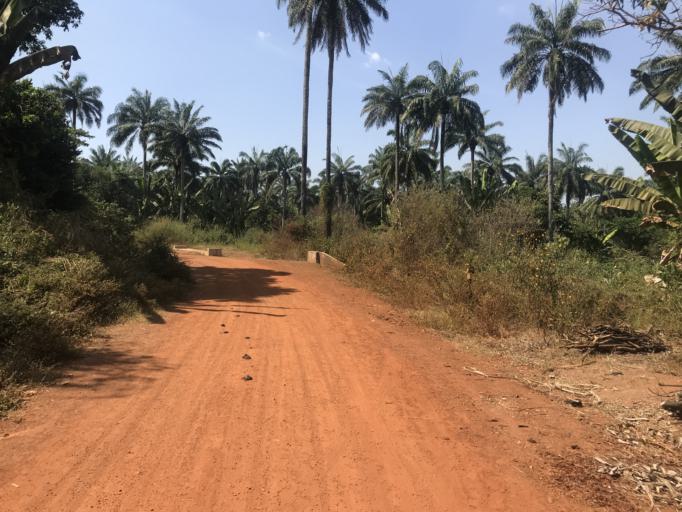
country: NG
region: Osun
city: Ikirun
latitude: 7.9338
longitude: 4.6341
